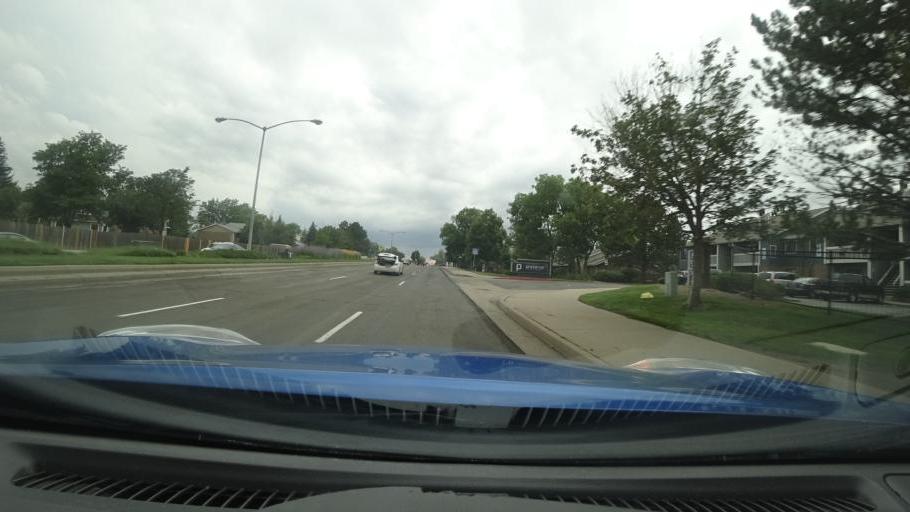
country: US
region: Colorado
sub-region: Adams County
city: Aurora
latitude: 39.6967
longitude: -104.8136
